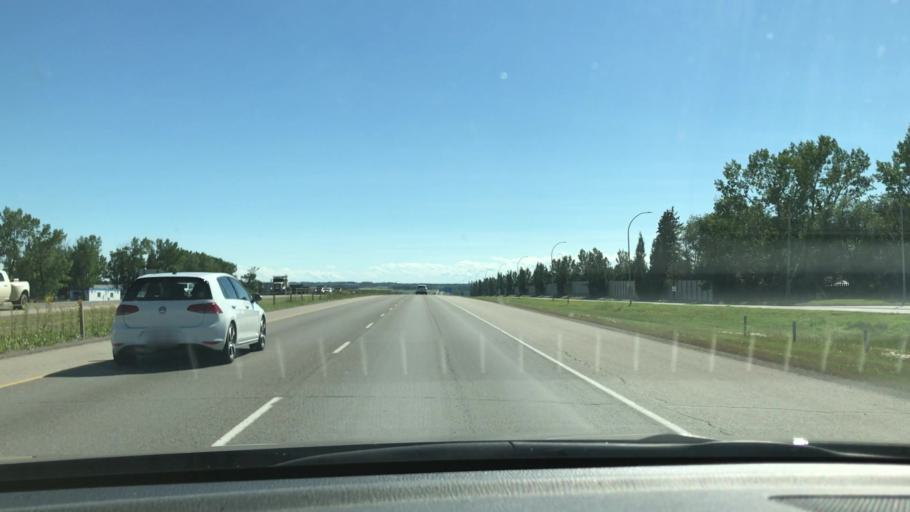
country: CA
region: Alberta
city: Penhold
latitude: 52.0148
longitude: -113.9459
